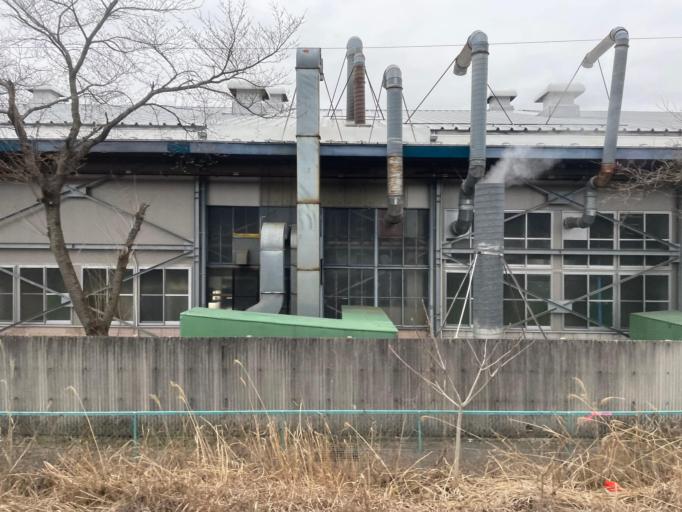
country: JP
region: Gunma
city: Numata
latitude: 36.6620
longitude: 139.0227
